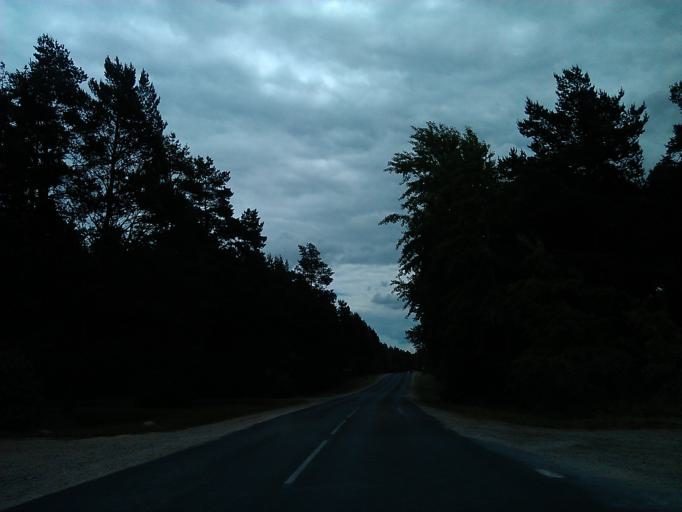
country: LV
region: Dobeles Rajons
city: Dobele
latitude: 56.6471
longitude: 23.2262
